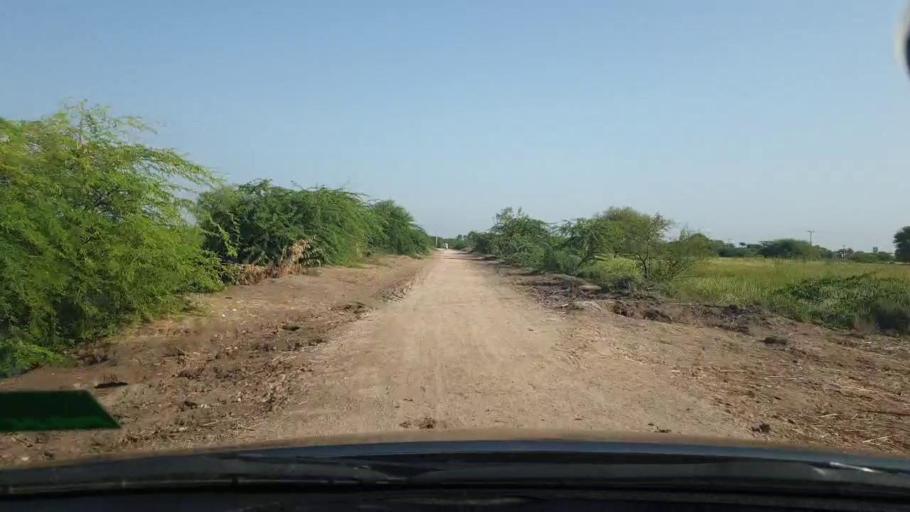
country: PK
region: Sindh
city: Tando Bago
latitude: 24.7195
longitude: 68.9533
